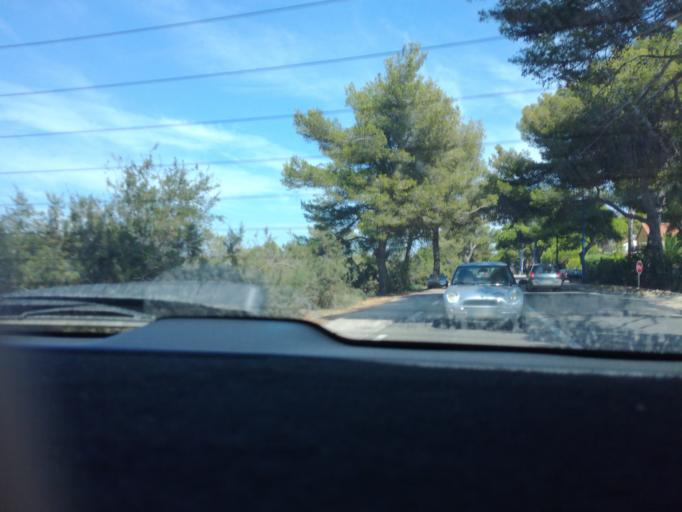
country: FR
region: Provence-Alpes-Cote d'Azur
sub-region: Departement du Var
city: Hyeres
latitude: 43.0614
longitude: 6.1471
